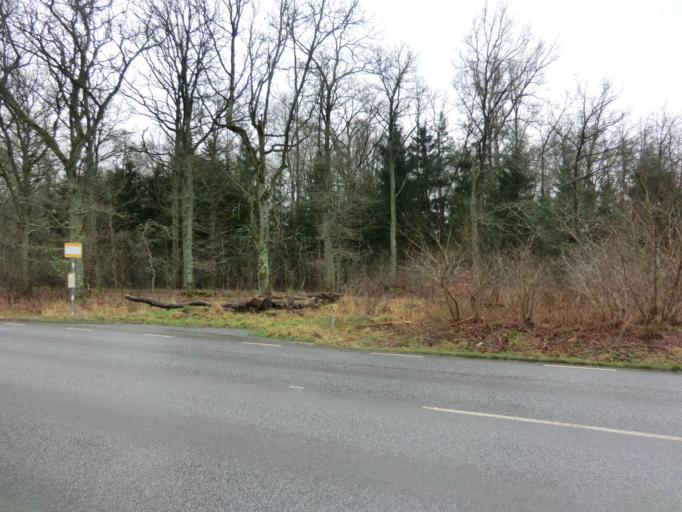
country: SE
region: Skane
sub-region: Hoors Kommun
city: Loberod
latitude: 55.7334
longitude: 13.3995
